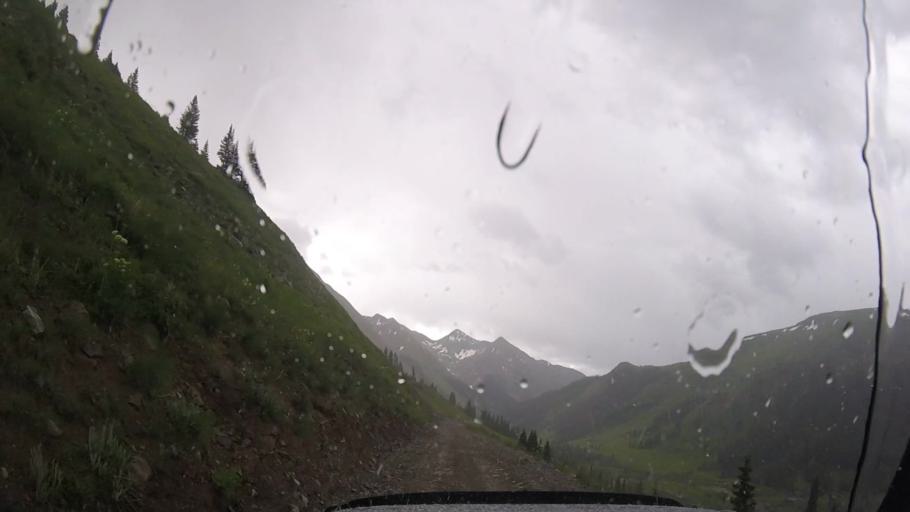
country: US
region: Colorado
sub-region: Ouray County
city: Ouray
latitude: 37.9351
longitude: -107.5696
